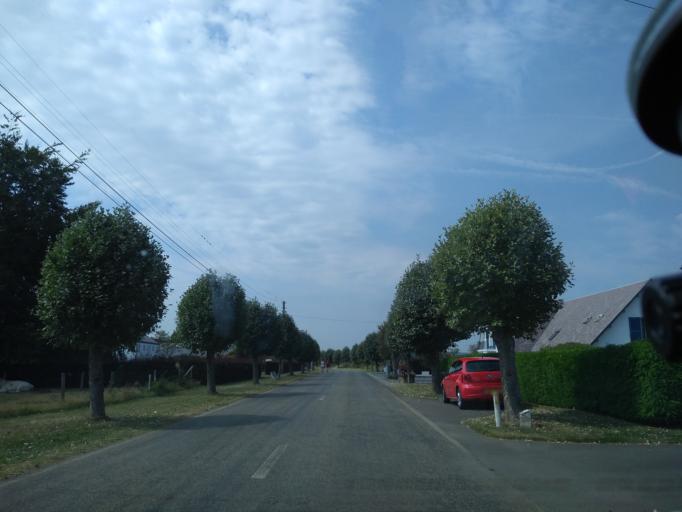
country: BE
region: Wallonia
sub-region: Province du Luxembourg
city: Bertogne
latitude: 50.1570
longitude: 5.6739
